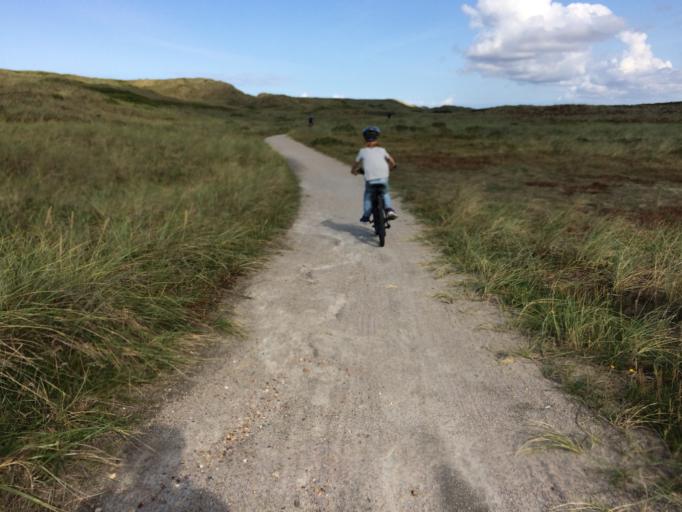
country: DK
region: Central Jutland
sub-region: Ringkobing-Skjern Kommune
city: Hvide Sande
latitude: 55.9407
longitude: 8.1491
